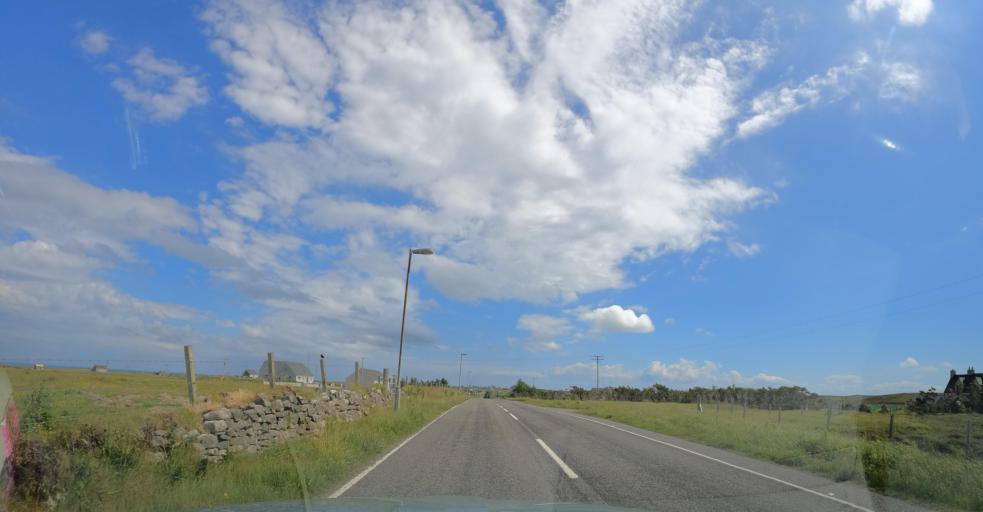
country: GB
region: Scotland
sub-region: Eilean Siar
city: Isle of Lewis
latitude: 58.4671
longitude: -6.2953
